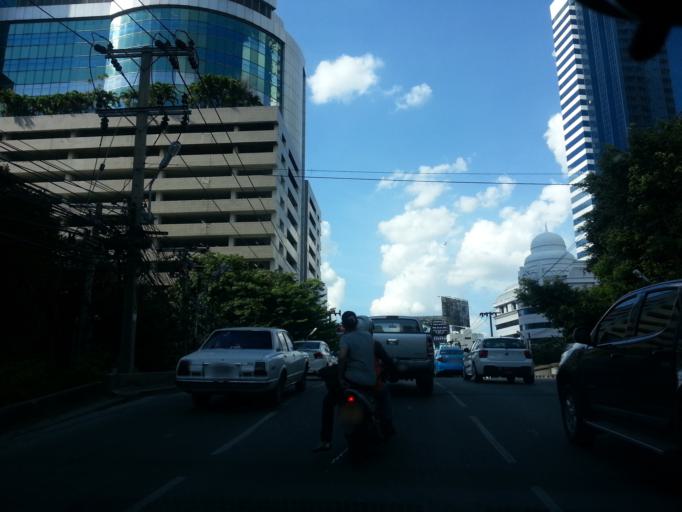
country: TH
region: Bangkok
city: Ratchathewi
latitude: 13.7480
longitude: 100.5483
